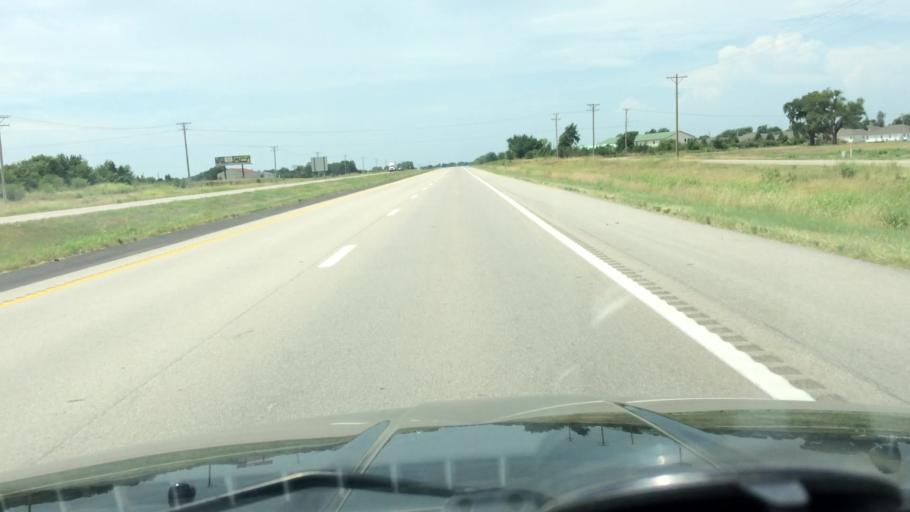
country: US
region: Missouri
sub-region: Polk County
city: Bolivar
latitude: 37.5846
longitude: -93.4157
